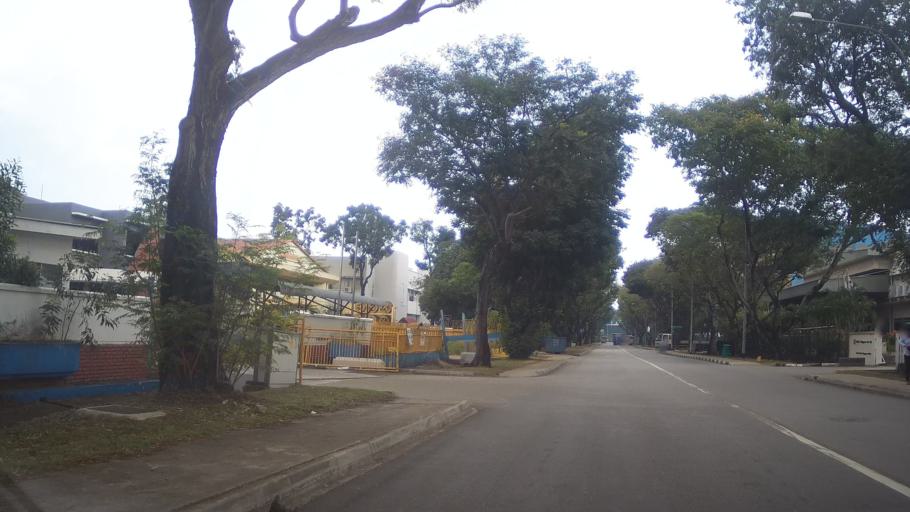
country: SG
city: Singapore
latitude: 1.3066
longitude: 103.6759
